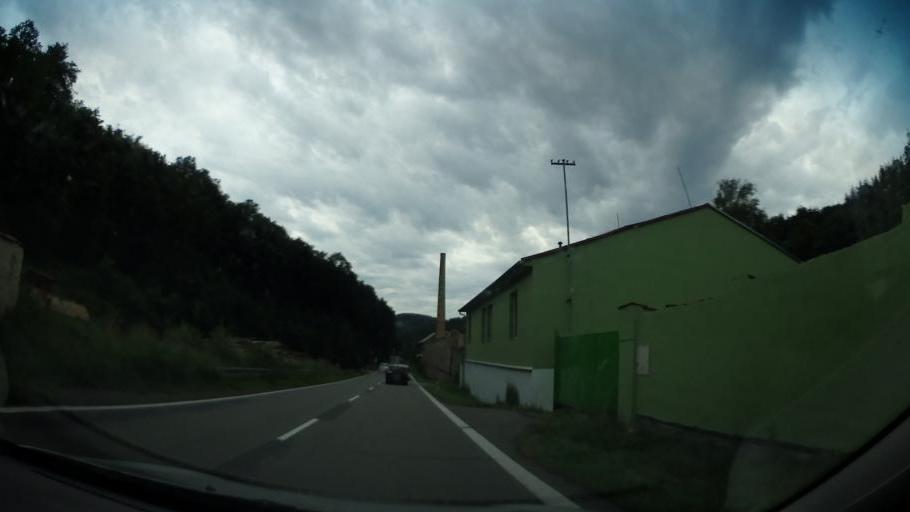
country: CZ
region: Pardubicky
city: Brnenec
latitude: 49.6104
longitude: 16.5323
